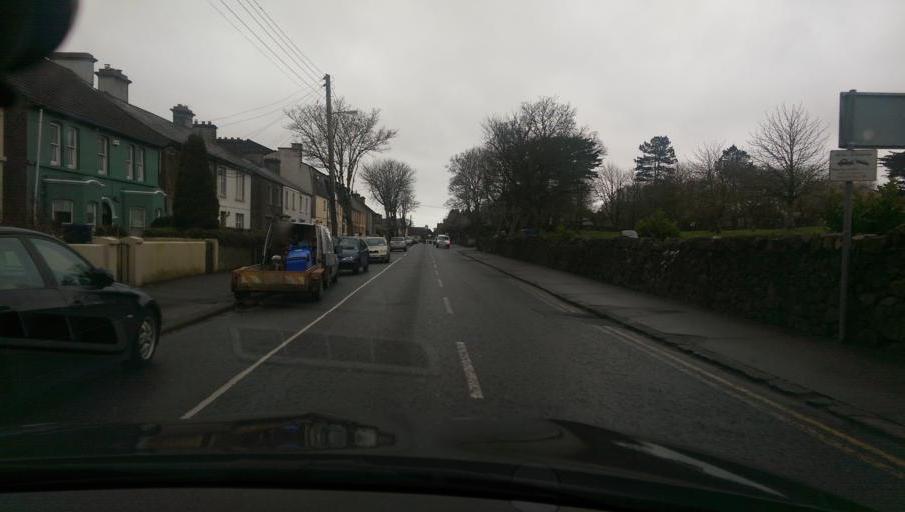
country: IE
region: Connaught
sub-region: County Galway
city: Gaillimh
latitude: 53.2709
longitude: -9.0641
